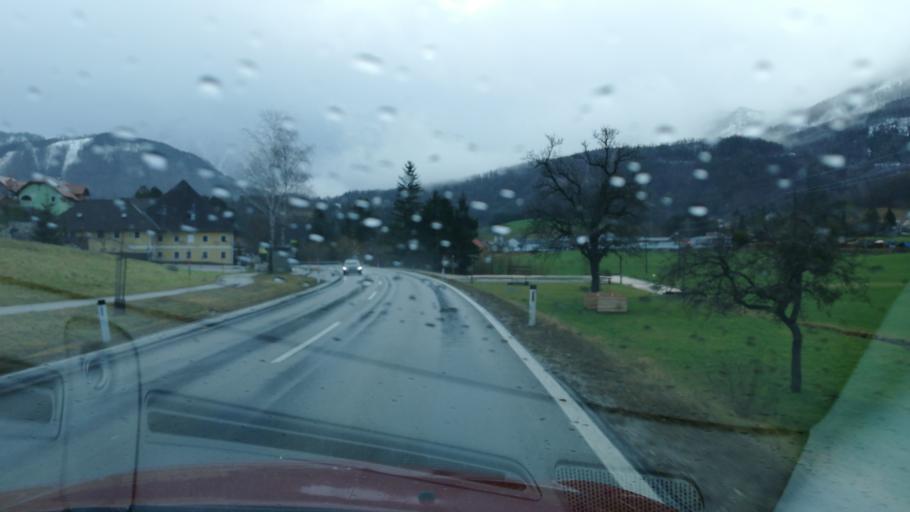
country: AT
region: Upper Austria
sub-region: Politischer Bezirk Kirchdorf an der Krems
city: Micheldorf in Oberoesterreich
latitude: 47.8555
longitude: 14.1500
